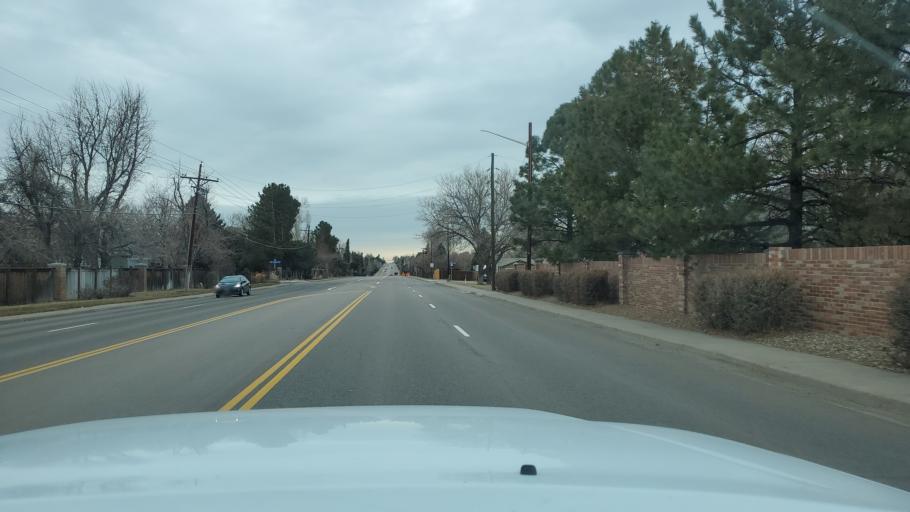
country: US
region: Colorado
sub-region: Arapahoe County
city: Southglenn
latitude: 39.5829
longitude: -104.9415
